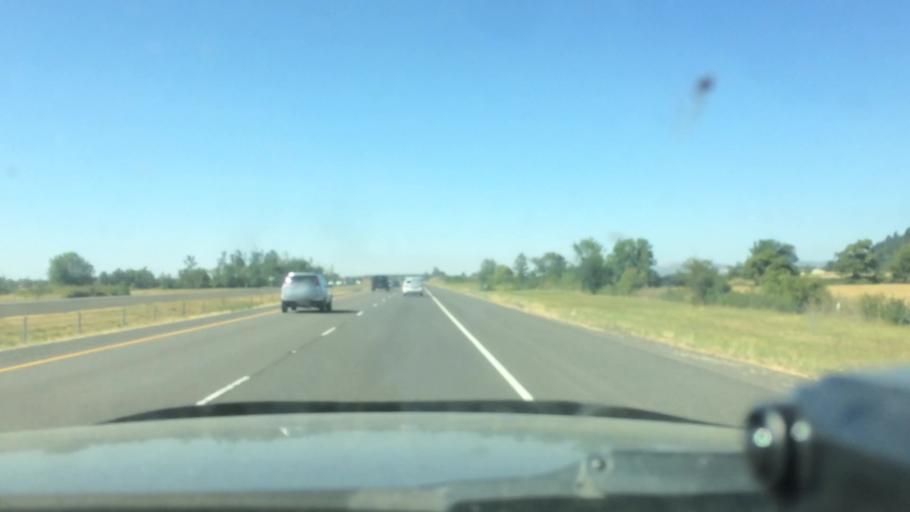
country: US
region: Oregon
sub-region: Lane County
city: Coburg
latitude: 44.1910
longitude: -123.0605
